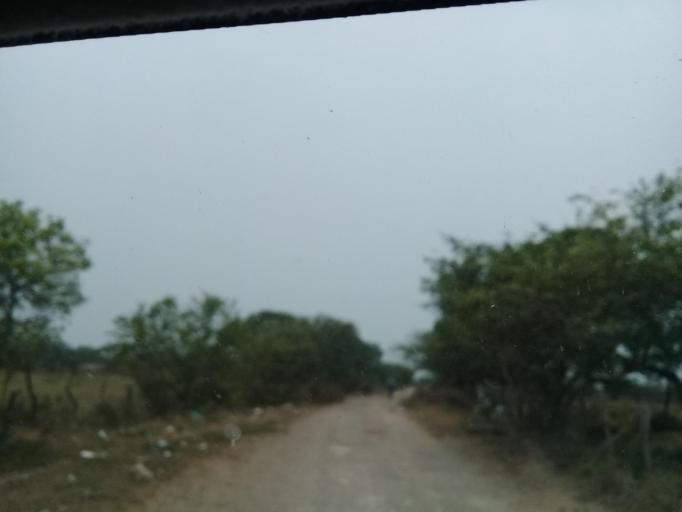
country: MX
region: Veracruz
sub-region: Veracruz
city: Las Amapolas
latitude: 19.1456
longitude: -96.2086
